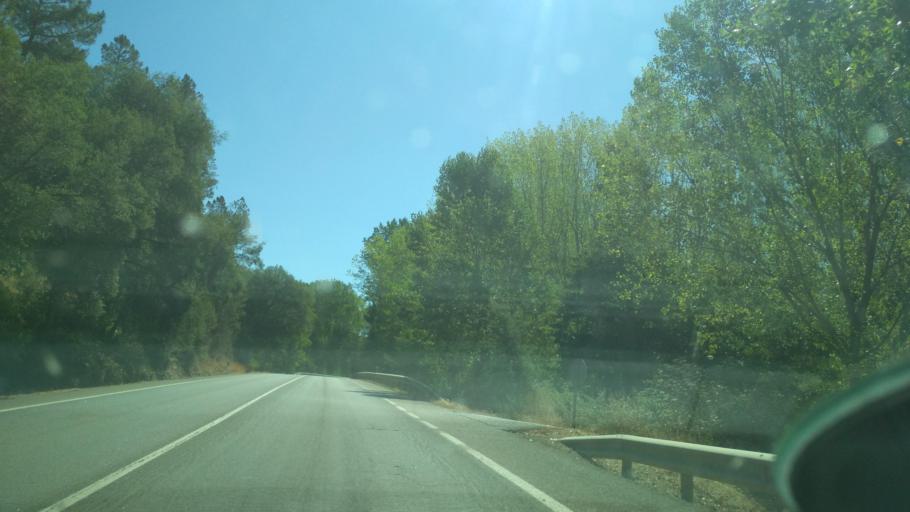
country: ES
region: Andalusia
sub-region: Provincia de Huelva
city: Fuenteheridos
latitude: 37.9166
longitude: -6.6827
